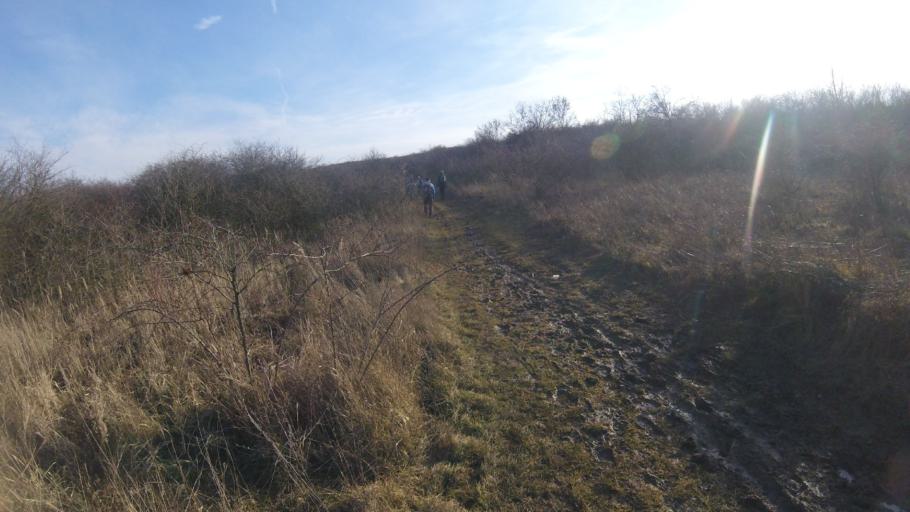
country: HU
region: Pest
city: Nagykovacsi
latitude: 47.6485
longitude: 18.9899
